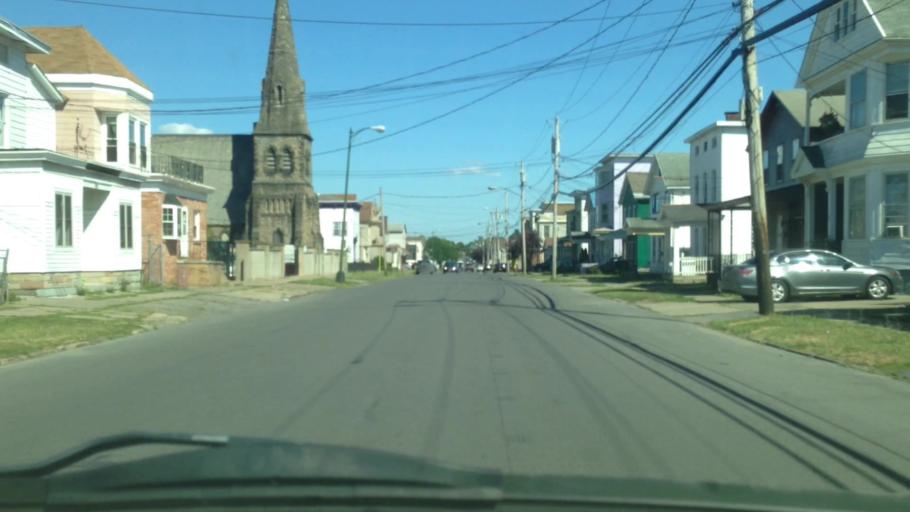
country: US
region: New York
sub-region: Oneida County
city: Utica
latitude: 43.0973
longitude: -75.2146
